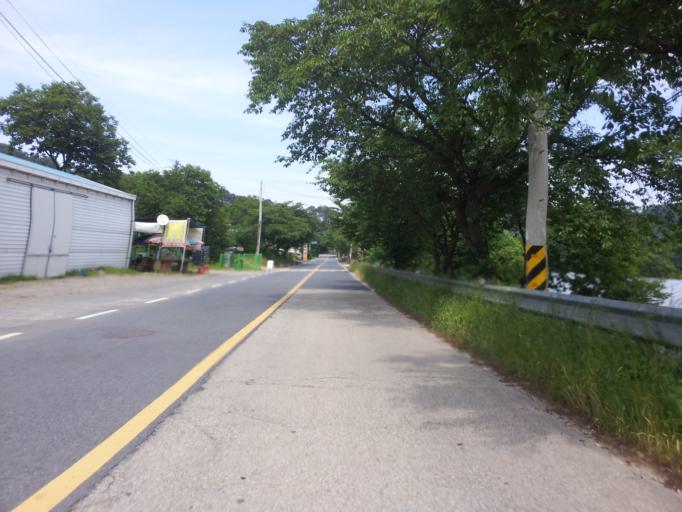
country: KR
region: Daejeon
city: Sintansin
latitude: 36.4264
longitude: 127.4644
